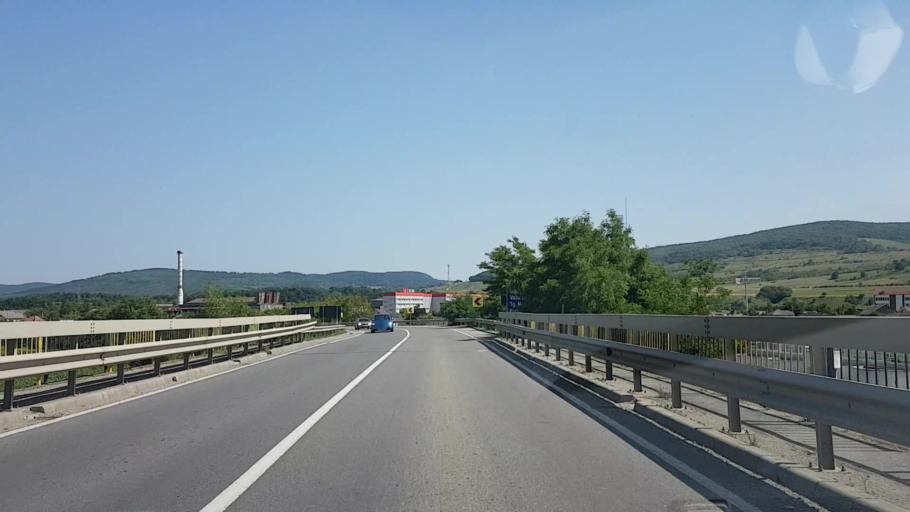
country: RO
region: Bistrita-Nasaud
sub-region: Comuna Beclean
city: Beclean
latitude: 47.1769
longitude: 24.1482
